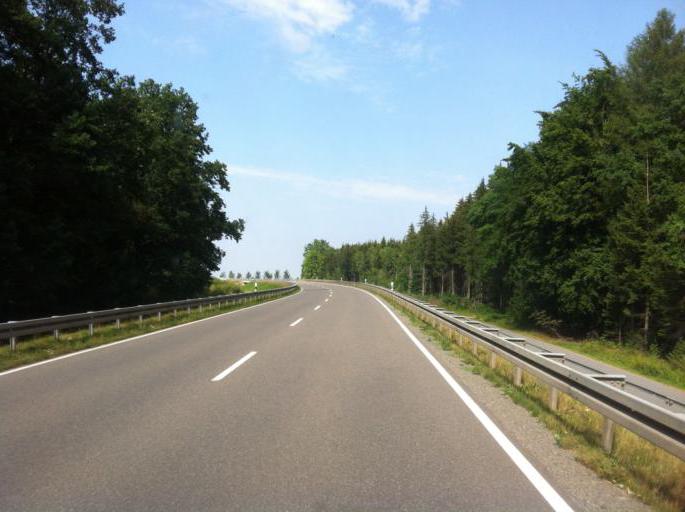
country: DE
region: Saxony
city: Neumark
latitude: 50.6292
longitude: 12.3418
